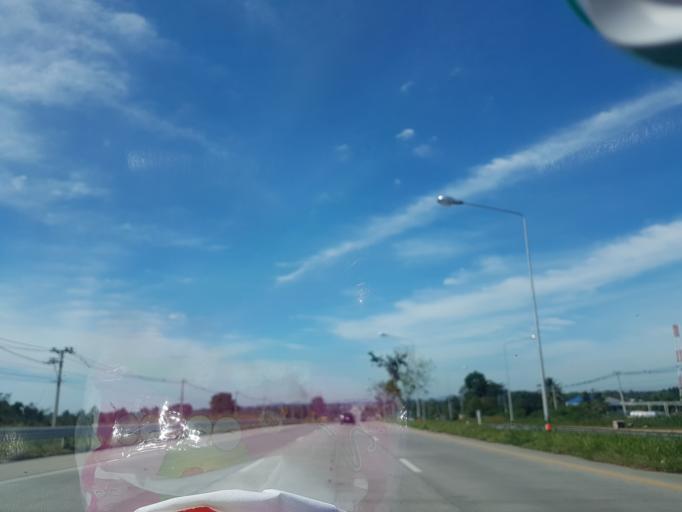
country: TH
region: Chon Buri
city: Phatthaya
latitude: 12.9302
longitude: 101.0014
